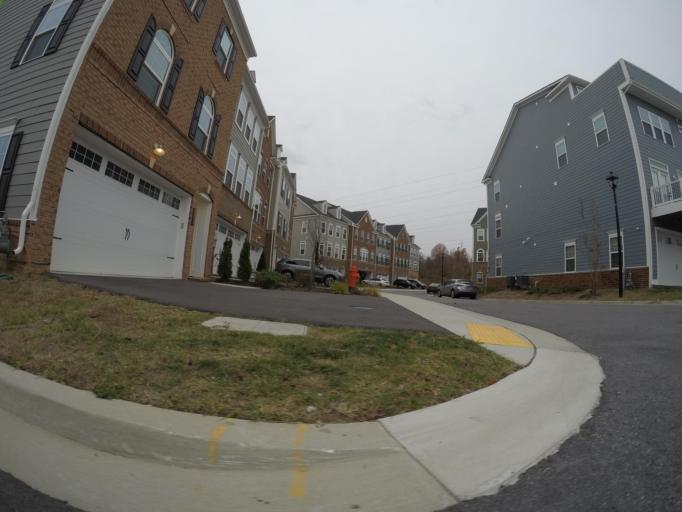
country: US
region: Maryland
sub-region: Howard County
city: Columbia
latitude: 39.2166
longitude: -76.7992
